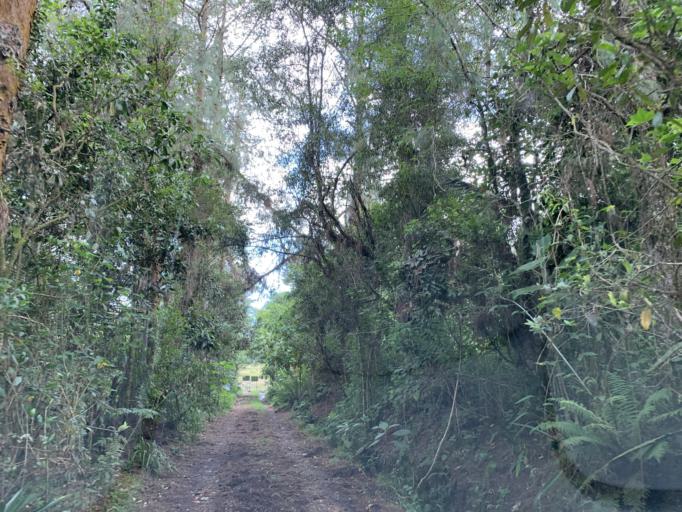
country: CO
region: Boyaca
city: Arcabuco
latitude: 5.7946
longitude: -73.4574
